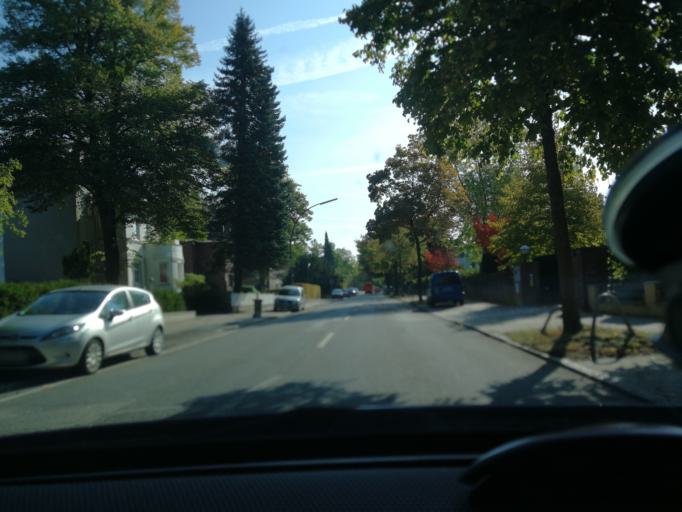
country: DE
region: Hamburg
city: Harburg
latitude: 53.4644
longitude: 9.9487
